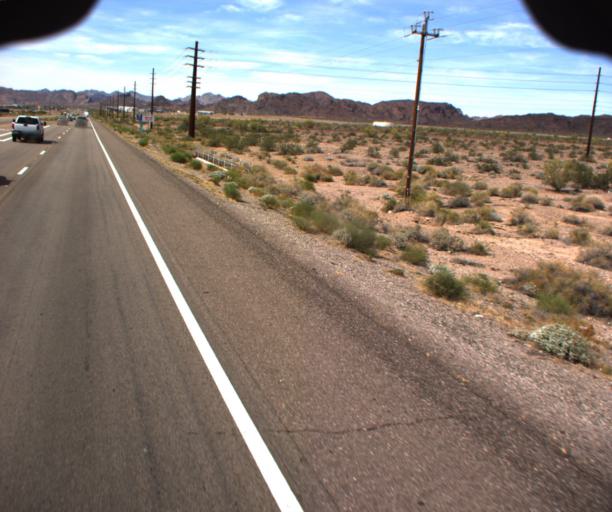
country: US
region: Arizona
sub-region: Mohave County
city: Desert Hills
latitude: 34.5526
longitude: -114.3573
